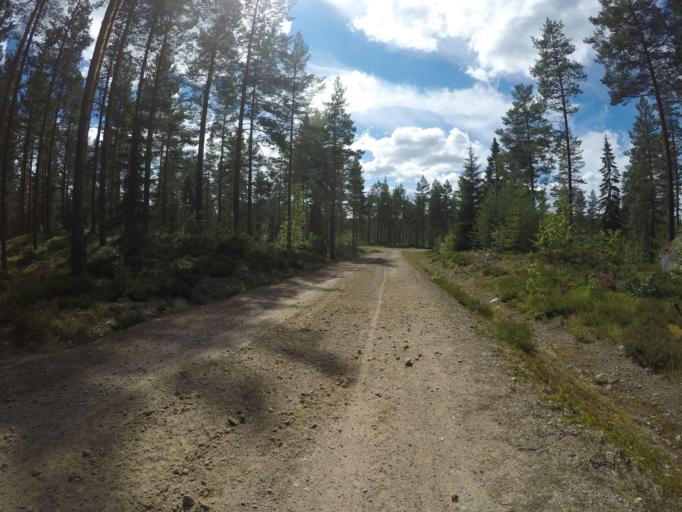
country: SE
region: Vaermland
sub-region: Filipstads Kommun
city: Lesjofors
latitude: 60.0783
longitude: 14.4394
